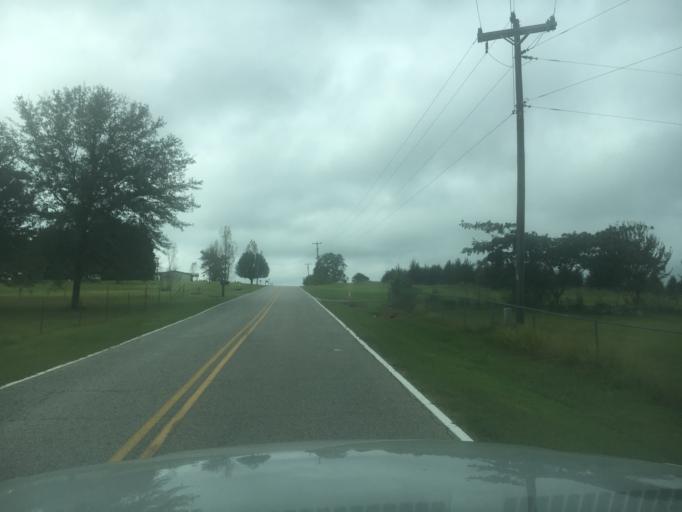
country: US
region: South Carolina
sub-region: Spartanburg County
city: Landrum
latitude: 35.1559
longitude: -82.1009
